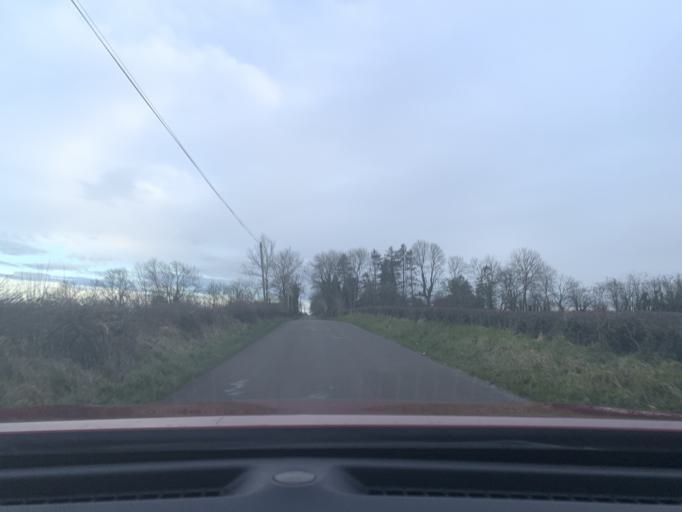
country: IE
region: Connaught
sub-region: Roscommon
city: Ballaghaderreen
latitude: 53.8773
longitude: -8.5615
